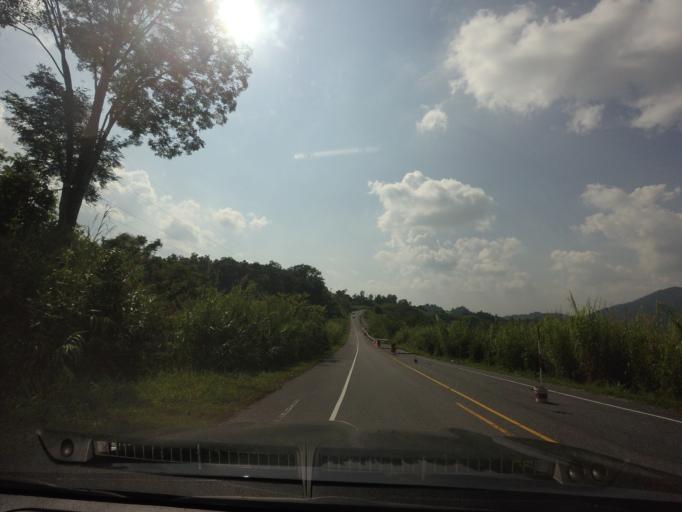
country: TH
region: Nan
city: Santi Suk
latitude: 18.9728
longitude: 101.0243
